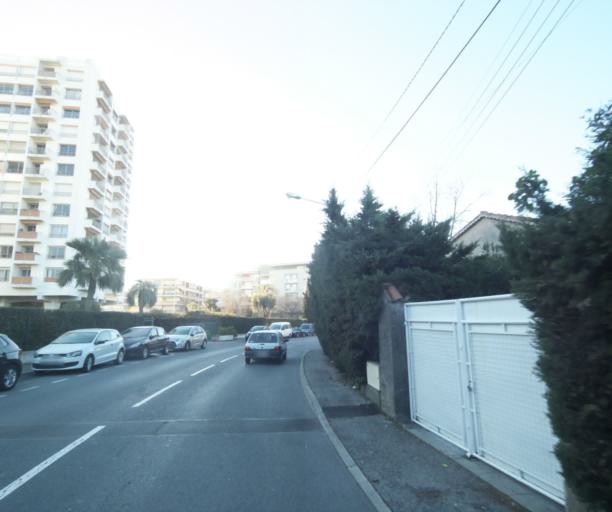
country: FR
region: Provence-Alpes-Cote d'Azur
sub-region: Departement des Alpes-Maritimes
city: Antibes
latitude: 43.5843
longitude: 7.1077
